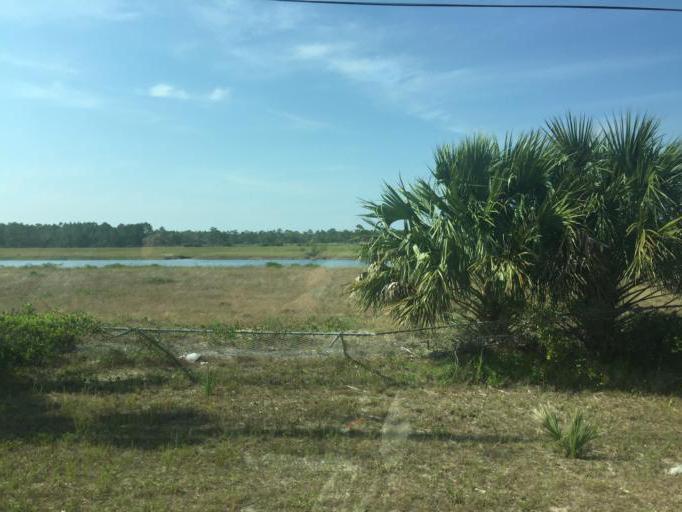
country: US
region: Florida
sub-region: Bay County
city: Panama City Beach
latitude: 30.1812
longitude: -85.7966
